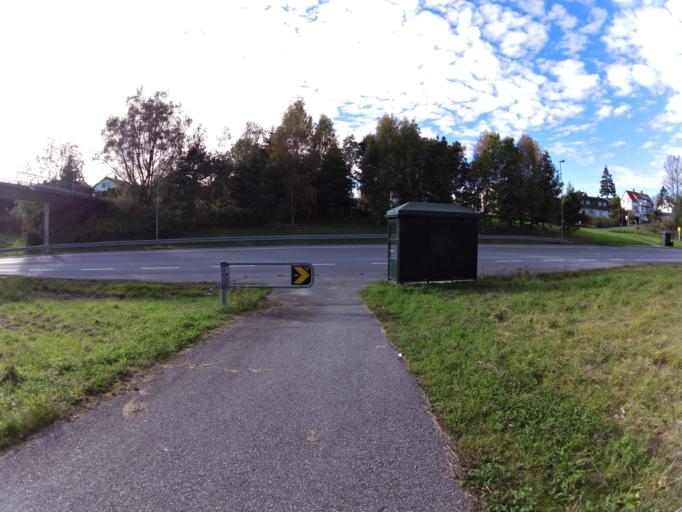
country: NO
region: Ostfold
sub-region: Sarpsborg
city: Sarpsborg
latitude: 59.2819
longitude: 11.0949
